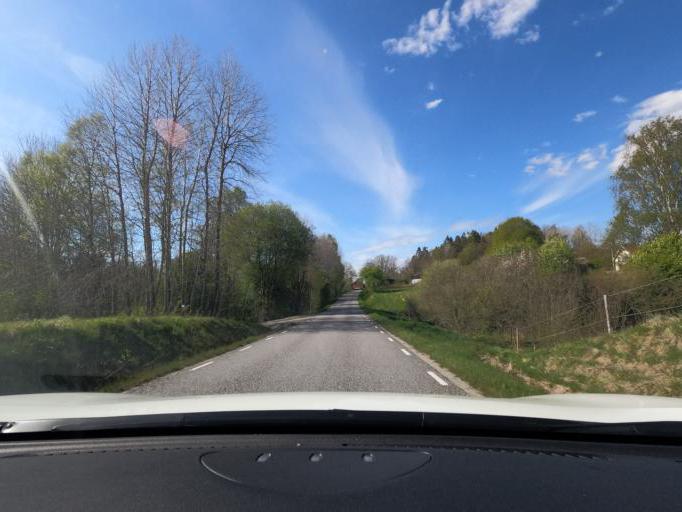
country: SE
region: Vaestra Goetaland
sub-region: Harryda Kommun
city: Ravlanda
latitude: 57.6303
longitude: 12.4992
